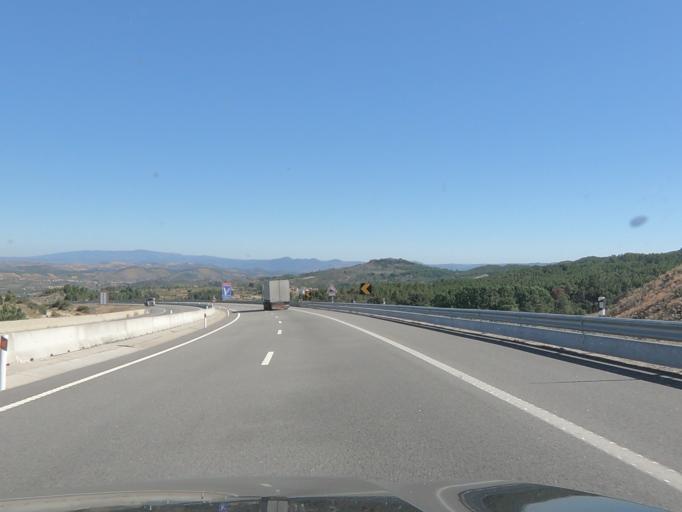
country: PT
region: Vila Real
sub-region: Murca
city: Murca
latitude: 41.3775
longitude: -7.4938
